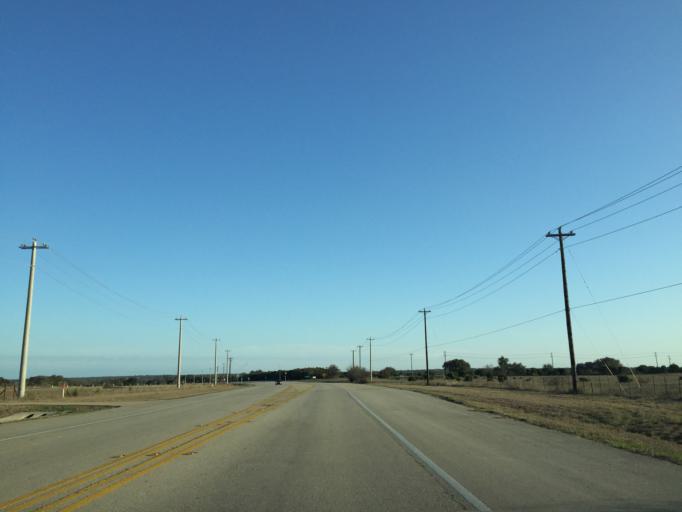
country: US
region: Texas
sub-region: Williamson County
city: Florence
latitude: 30.7437
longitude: -97.8032
